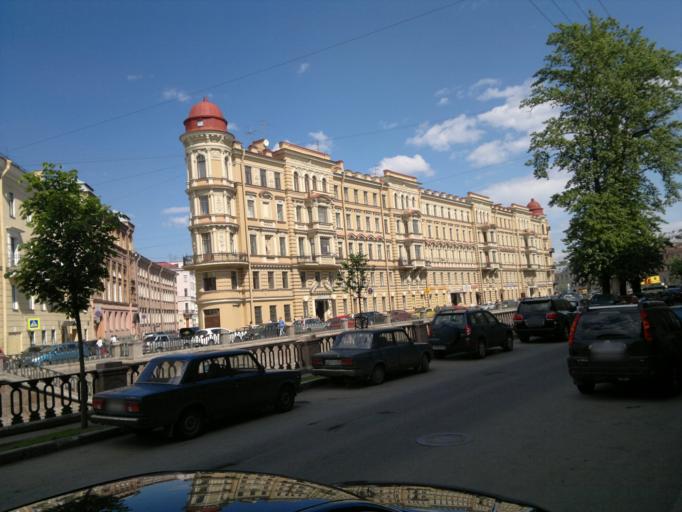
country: RU
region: St.-Petersburg
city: Saint Petersburg
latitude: 59.9260
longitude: 30.3102
